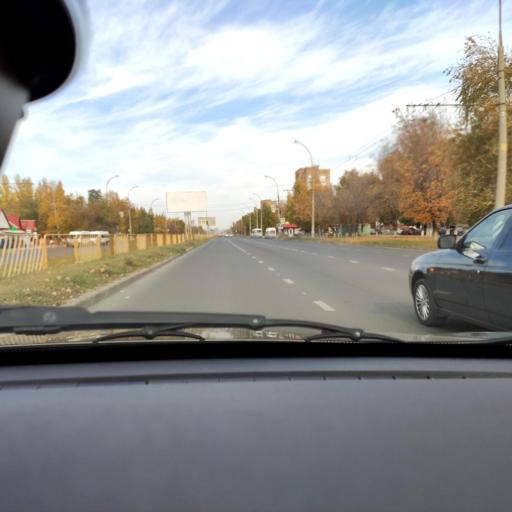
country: RU
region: Samara
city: Tol'yatti
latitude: 53.5292
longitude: 49.2975
